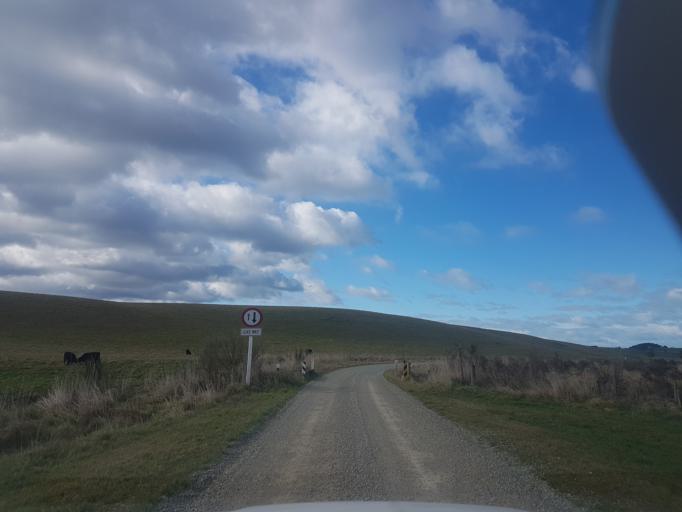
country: NZ
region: Canterbury
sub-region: Timaru District
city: Pleasant Point
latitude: -44.1872
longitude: 171.1883
